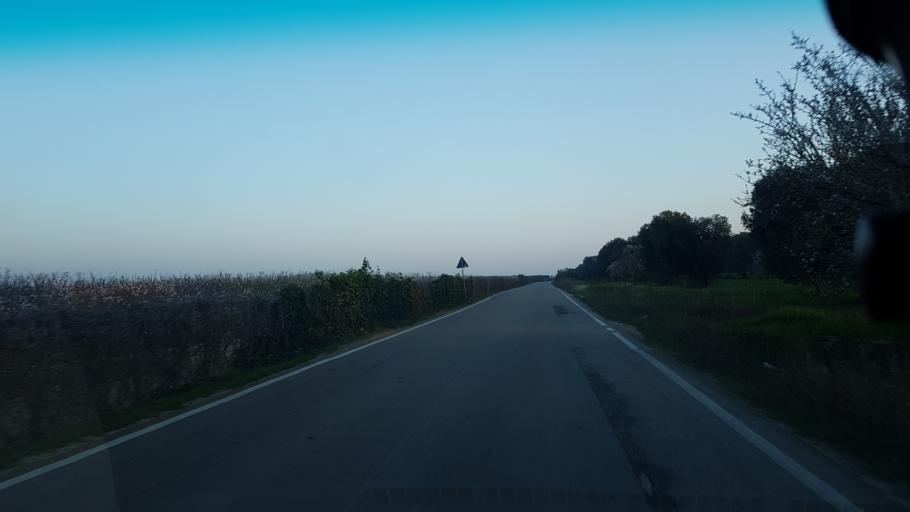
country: IT
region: Apulia
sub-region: Provincia di Brindisi
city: San Vito dei Normanni
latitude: 40.6361
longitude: 17.7810
